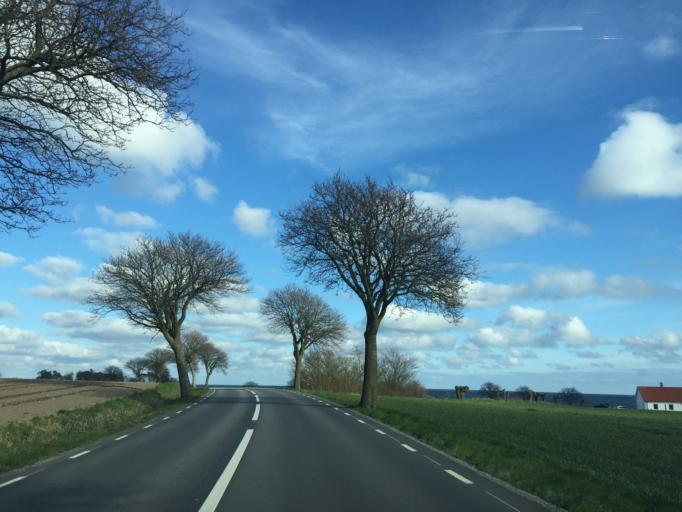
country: SE
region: Skane
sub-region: Skurups Kommun
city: Skivarp
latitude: 55.4186
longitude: 13.6319
